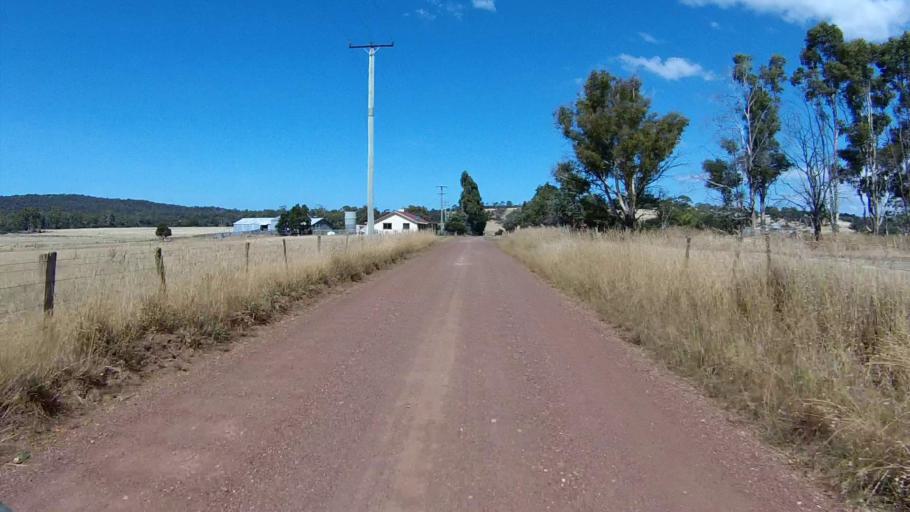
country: AU
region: Tasmania
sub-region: Break O'Day
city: St Helens
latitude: -41.9612
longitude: 148.0699
